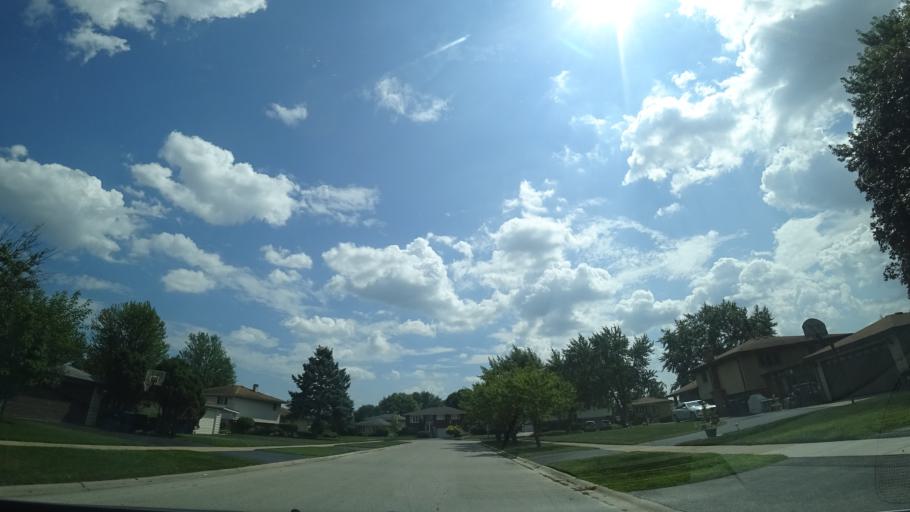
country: US
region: Illinois
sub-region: Cook County
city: Alsip
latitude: 41.6744
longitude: -87.7245
